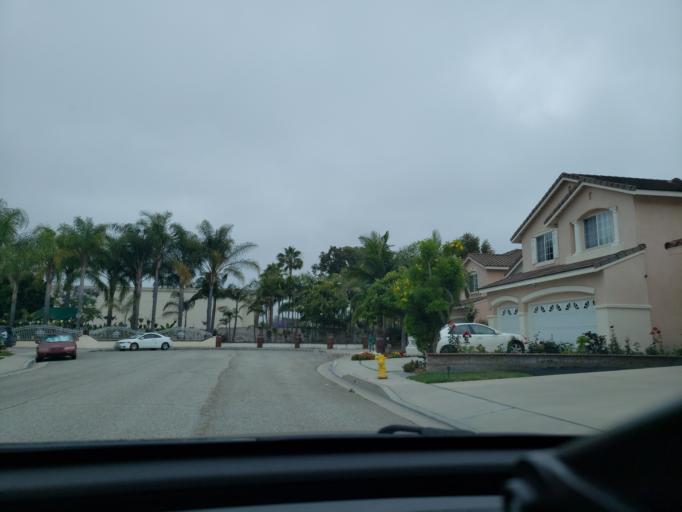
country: US
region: California
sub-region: Los Angeles County
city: Artesia
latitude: 33.8607
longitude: -118.0879
